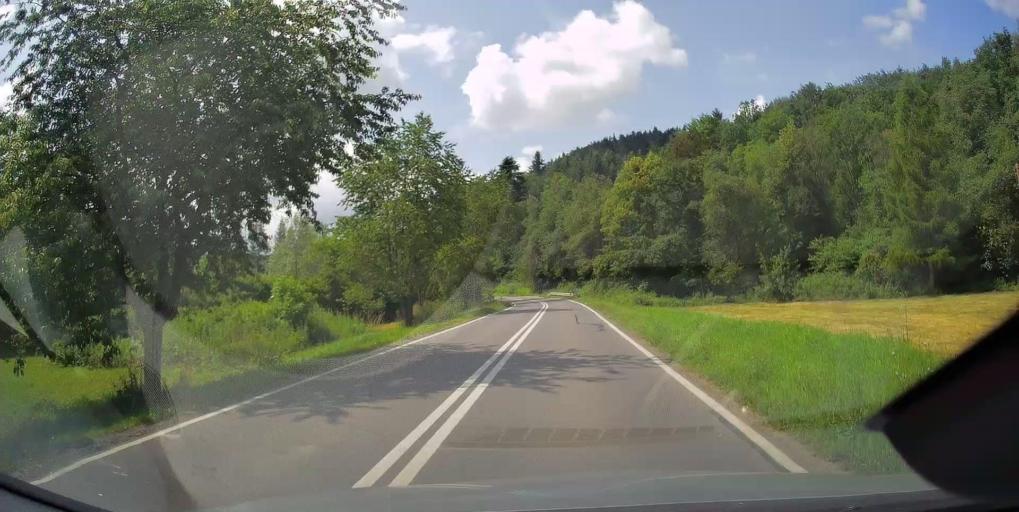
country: PL
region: Lesser Poland Voivodeship
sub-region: Powiat tarnowski
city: Zakliczyn
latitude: 49.8205
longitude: 20.7998
